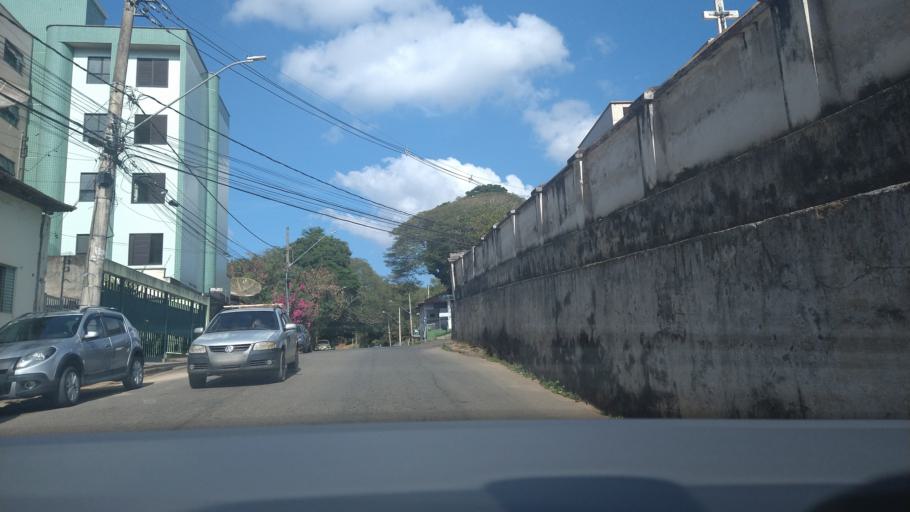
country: BR
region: Minas Gerais
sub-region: Vicosa
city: Vicosa
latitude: -20.7578
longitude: -42.8768
